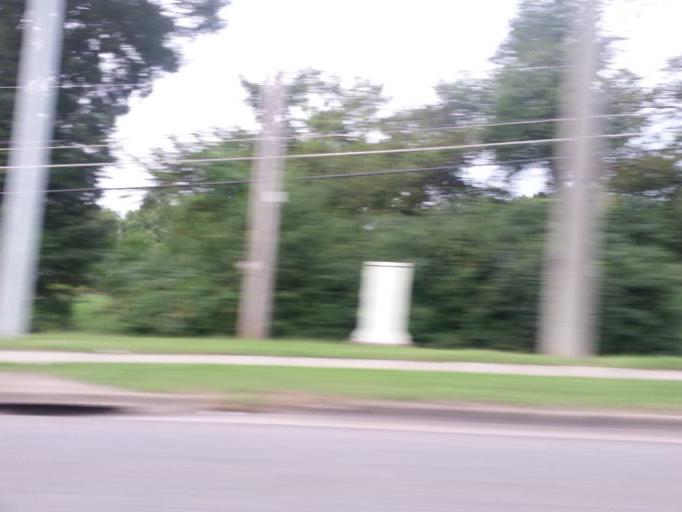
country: US
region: Alabama
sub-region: Madison County
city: Huntsville
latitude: 34.7350
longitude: -86.6167
